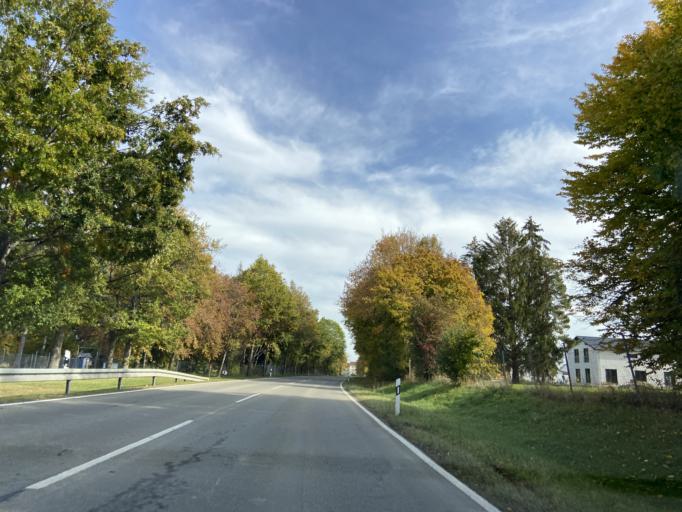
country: DE
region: Baden-Wuerttemberg
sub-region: Tuebingen Region
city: Stetten am Kalten Markt
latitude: 48.1255
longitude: 9.0709
